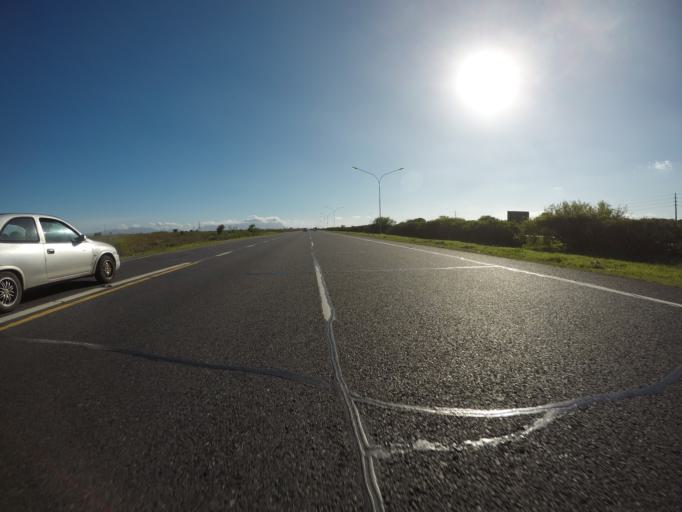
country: ZA
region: Western Cape
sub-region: City of Cape Town
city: Kraaifontein
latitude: -34.0246
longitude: 18.6857
